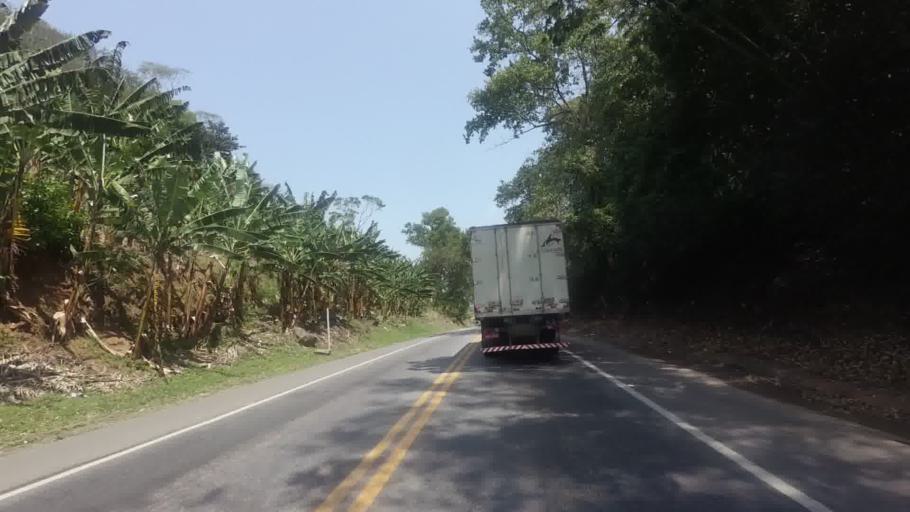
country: BR
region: Espirito Santo
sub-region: Iconha
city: Iconha
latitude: -20.7971
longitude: -40.8211
